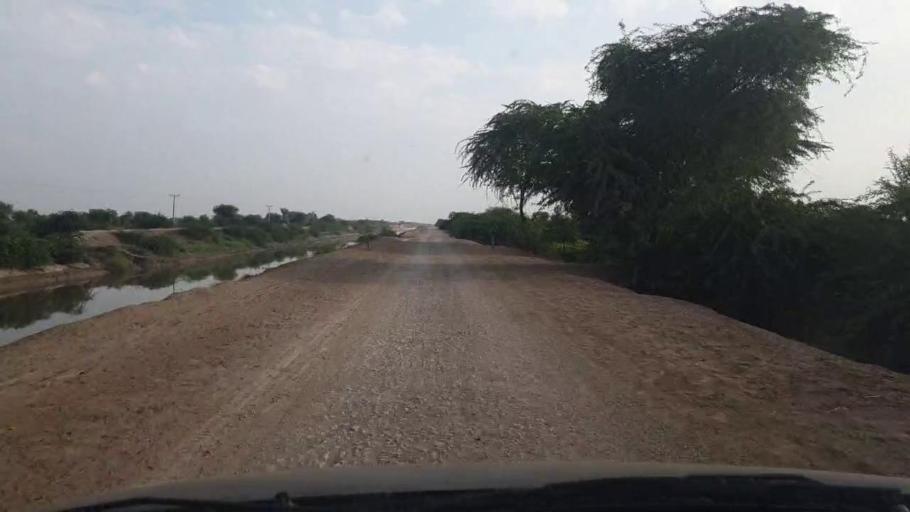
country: PK
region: Sindh
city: Badin
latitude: 24.5190
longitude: 68.6830
